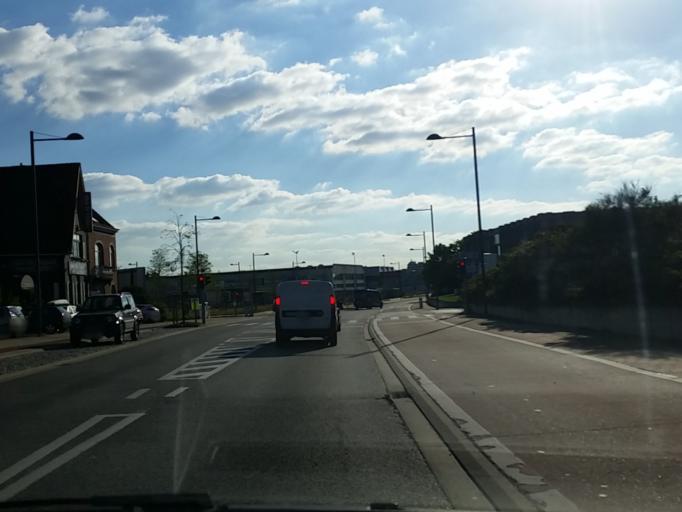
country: BE
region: Flanders
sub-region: Provincie Vlaams-Brabant
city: Diegem
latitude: 50.8851
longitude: 4.4222
